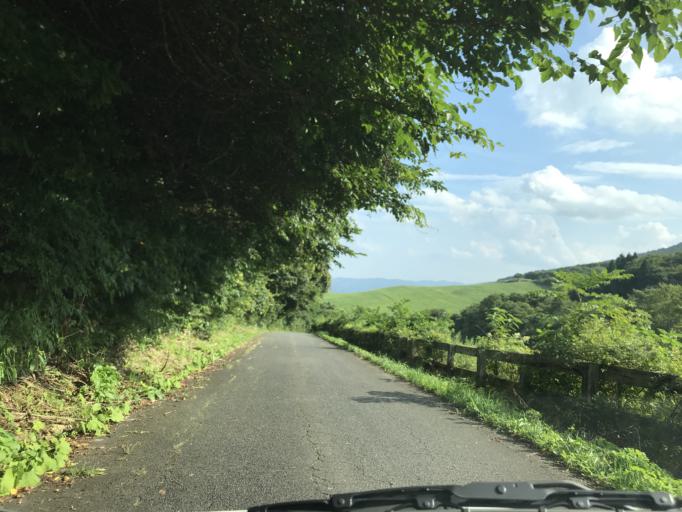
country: JP
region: Iwate
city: Ofunato
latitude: 38.9877
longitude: 141.4636
